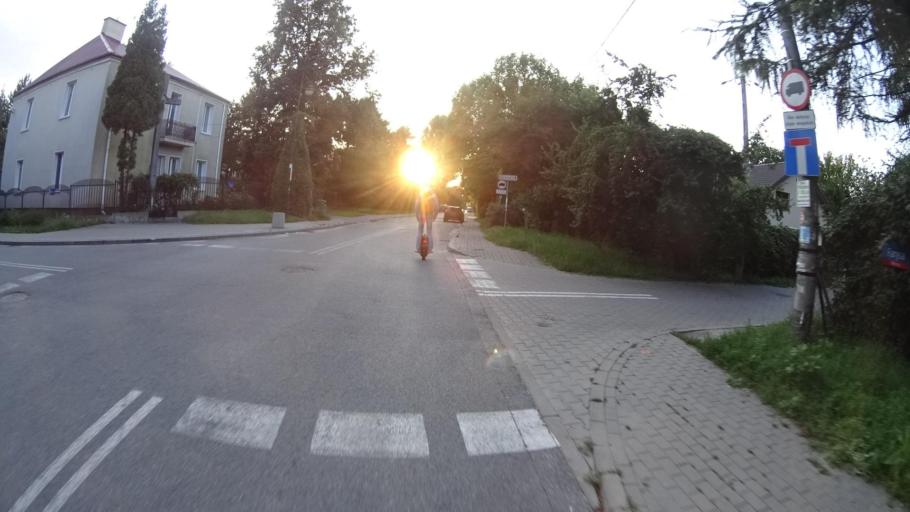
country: PL
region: Masovian Voivodeship
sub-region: Warszawa
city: Bielany
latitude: 52.3048
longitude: 20.9416
